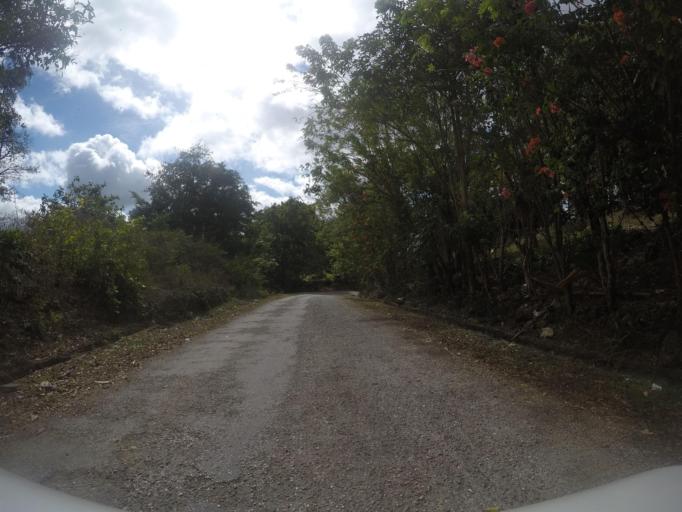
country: TL
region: Lautem
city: Lospalos
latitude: -8.5395
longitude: 126.9398
